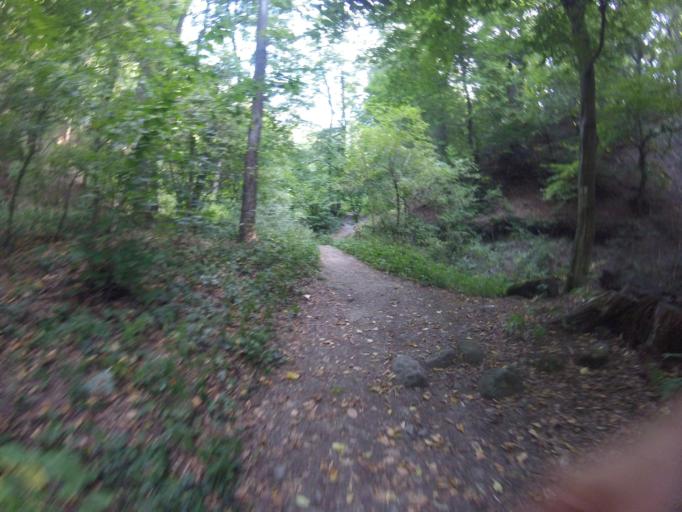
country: HU
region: Pest
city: Csobanka
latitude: 47.6686
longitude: 18.9666
